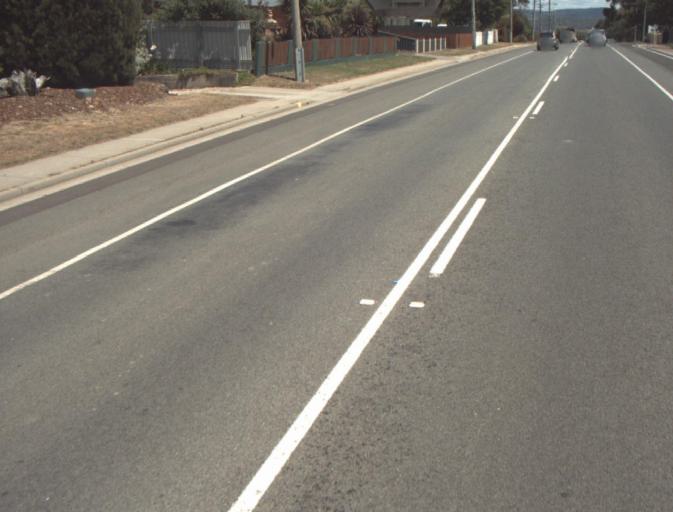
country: AU
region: Tasmania
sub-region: Launceston
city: Mayfield
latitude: -41.3743
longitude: 147.1343
